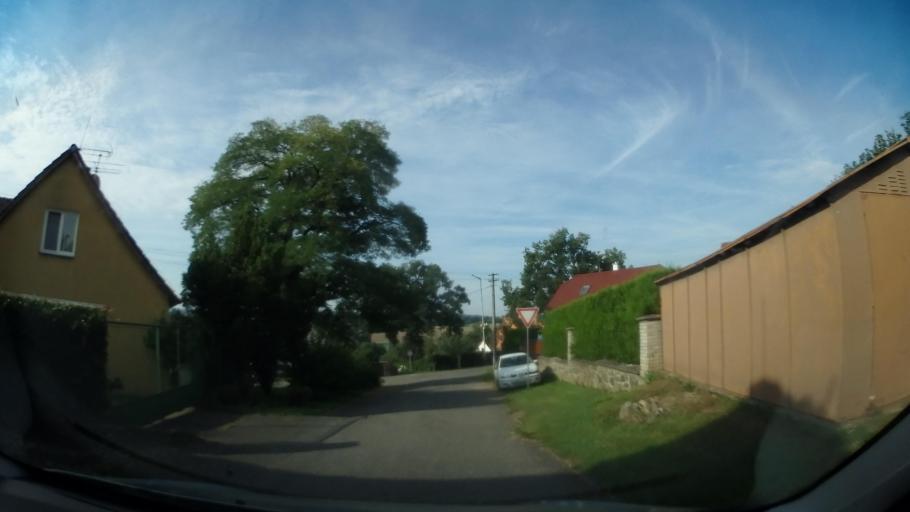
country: CZ
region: Jihocesky
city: Cimelice
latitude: 49.4215
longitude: 14.1194
